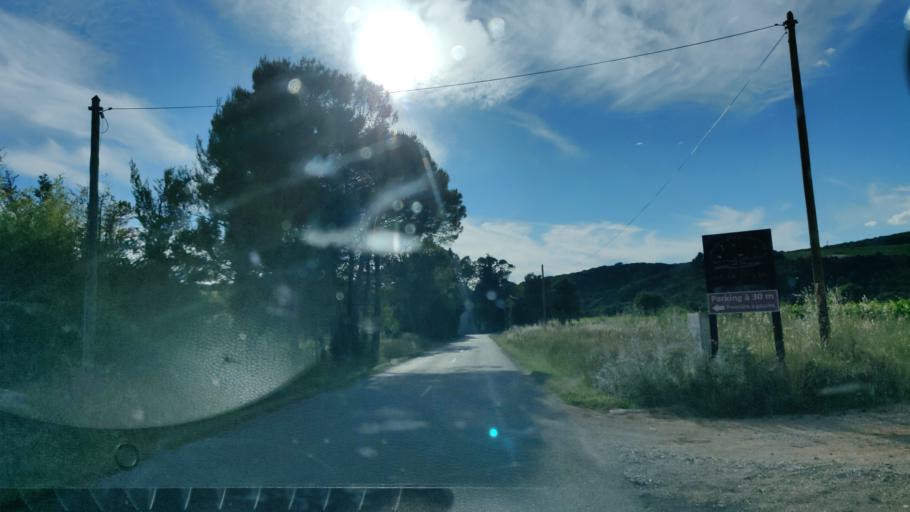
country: FR
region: Languedoc-Roussillon
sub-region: Departement de l'Herault
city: Combaillaux
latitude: 43.6630
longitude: 3.7684
